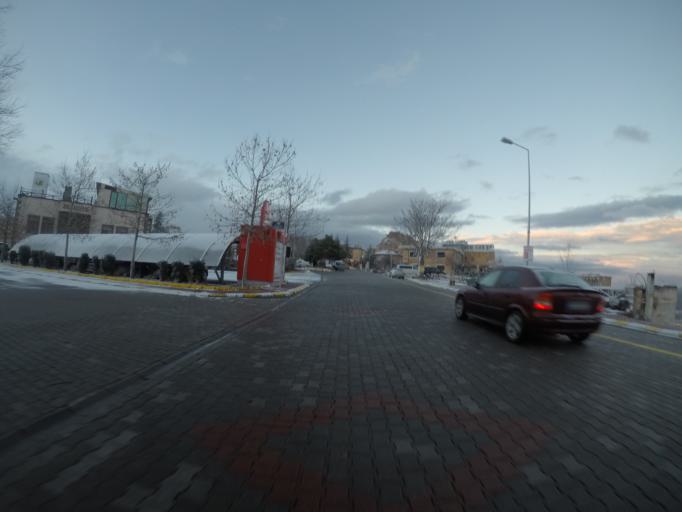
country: TR
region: Nevsehir
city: Goereme
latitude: 38.6267
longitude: 34.8045
